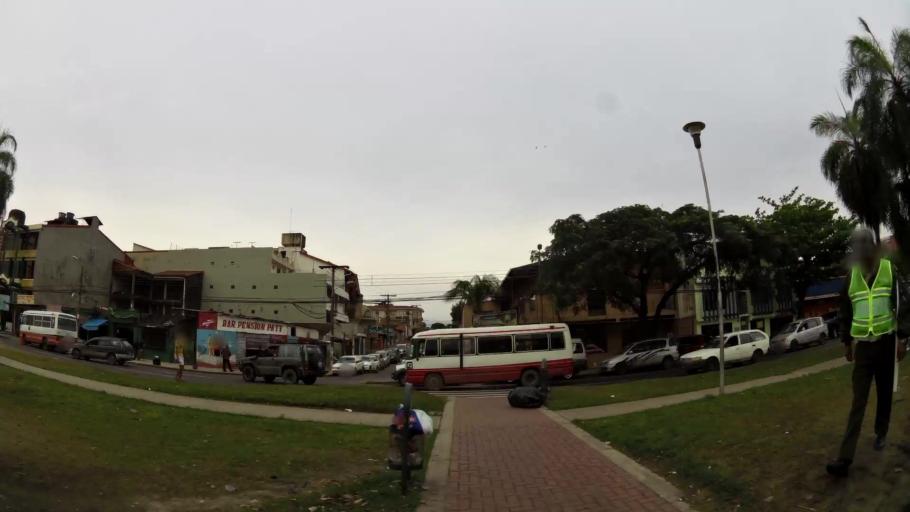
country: BO
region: Santa Cruz
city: Santa Cruz de la Sierra
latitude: -17.7945
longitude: -63.1867
